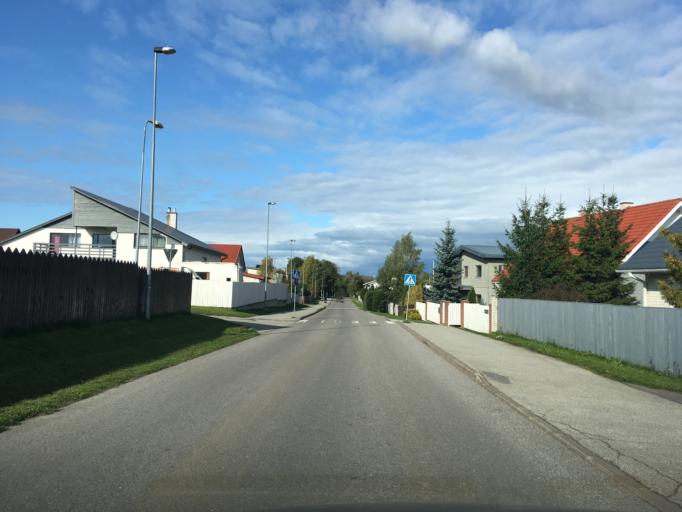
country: EE
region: Harju
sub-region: Saue vald
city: Laagri
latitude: 59.3476
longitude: 24.6407
